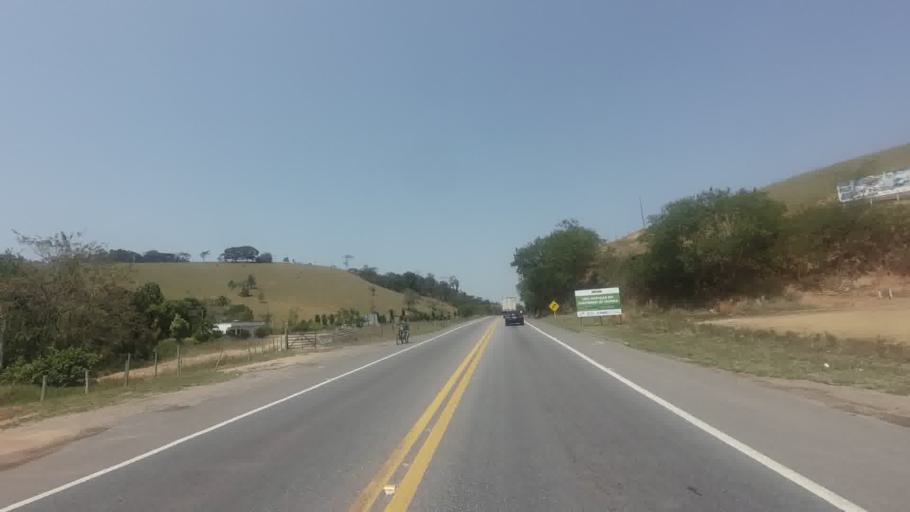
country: BR
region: Espirito Santo
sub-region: Iconha
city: Iconha
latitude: -20.7787
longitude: -40.7802
